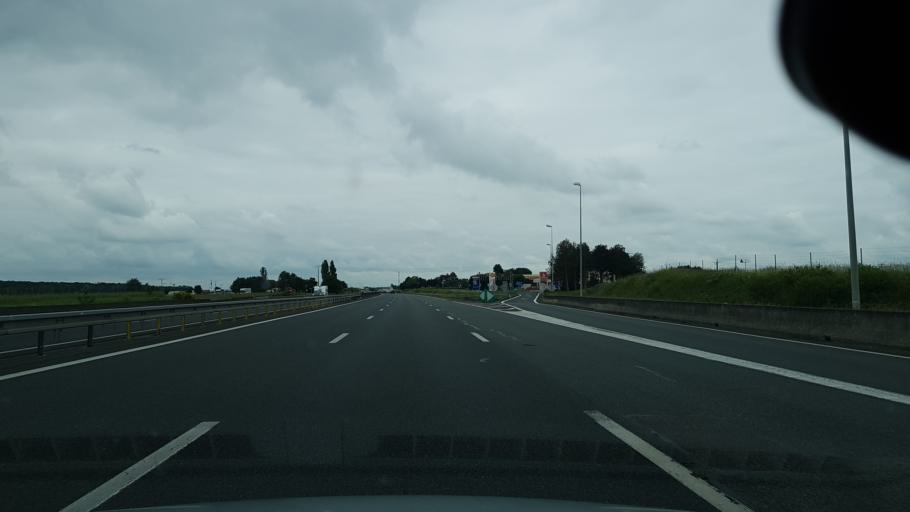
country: FR
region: Centre
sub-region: Departement du Loir-et-Cher
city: La Chaussee-Saint-Victor
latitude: 47.6678
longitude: 1.3905
